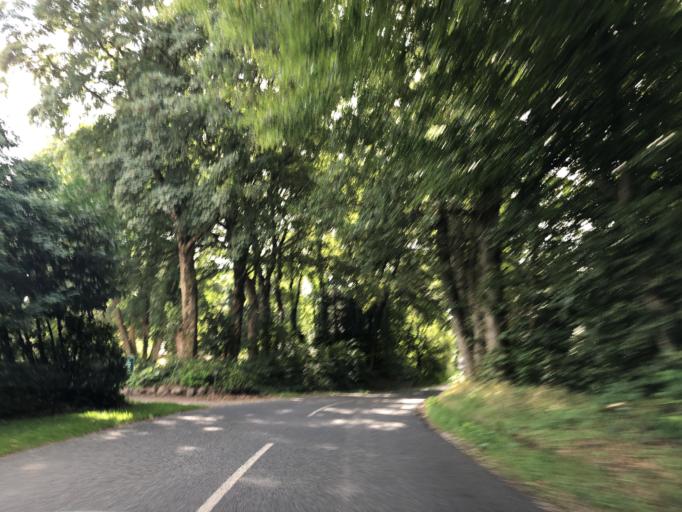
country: DK
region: North Denmark
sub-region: Vesthimmerland Kommune
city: Alestrup
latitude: 56.6054
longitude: 9.4345
